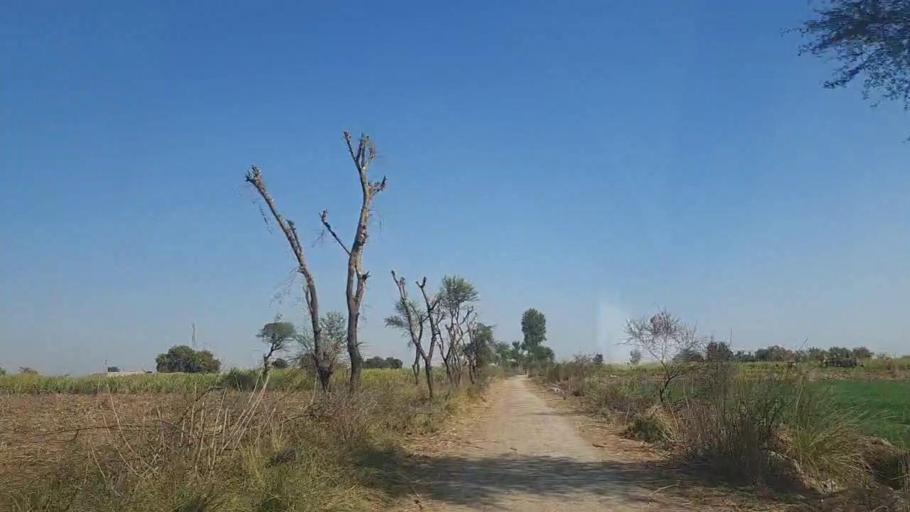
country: PK
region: Sindh
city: Sanghar
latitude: 26.2262
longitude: 68.9660
